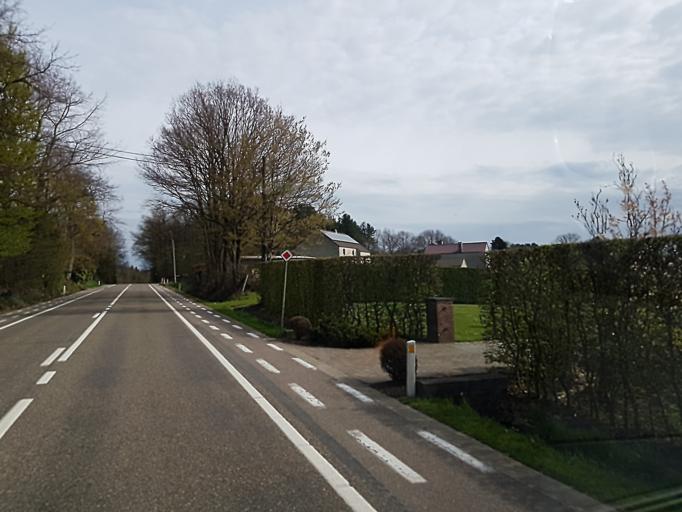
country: BE
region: Flanders
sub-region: Provincie Antwerpen
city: Herselt
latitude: 51.0314
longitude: 4.8489
